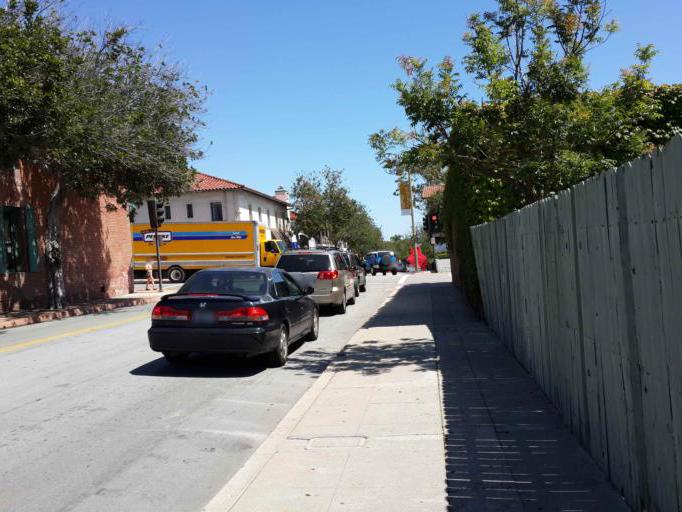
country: US
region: California
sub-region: San Luis Obispo County
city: San Luis Obispo
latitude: 35.2817
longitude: -120.6646
